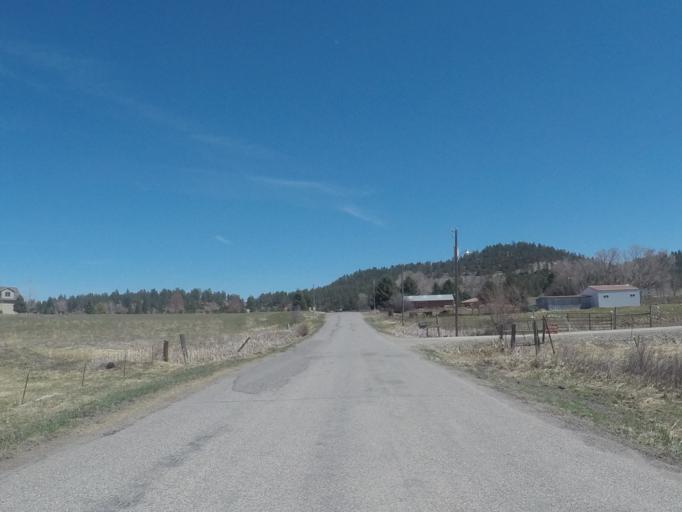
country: US
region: Montana
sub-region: Stillwater County
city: Columbus
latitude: 45.6240
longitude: -109.2833
